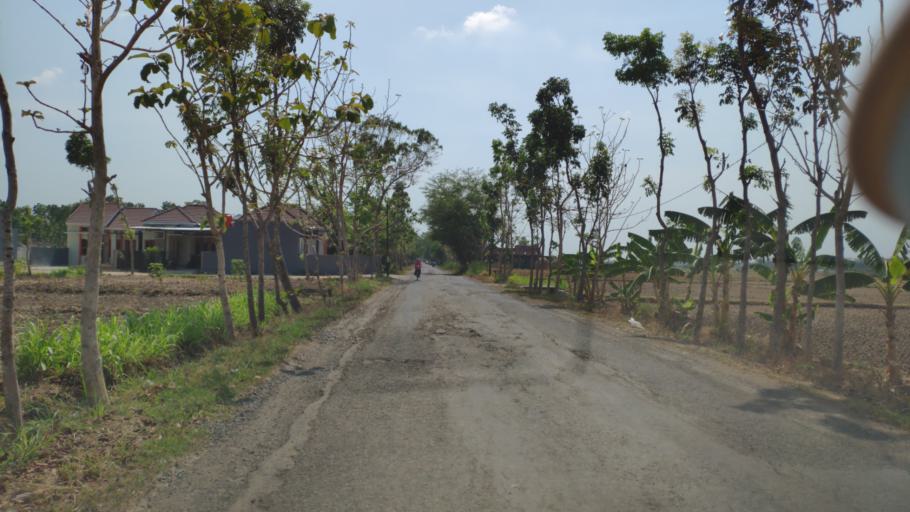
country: ID
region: Central Java
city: Kedungjenar
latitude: -6.9805
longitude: 111.4276
